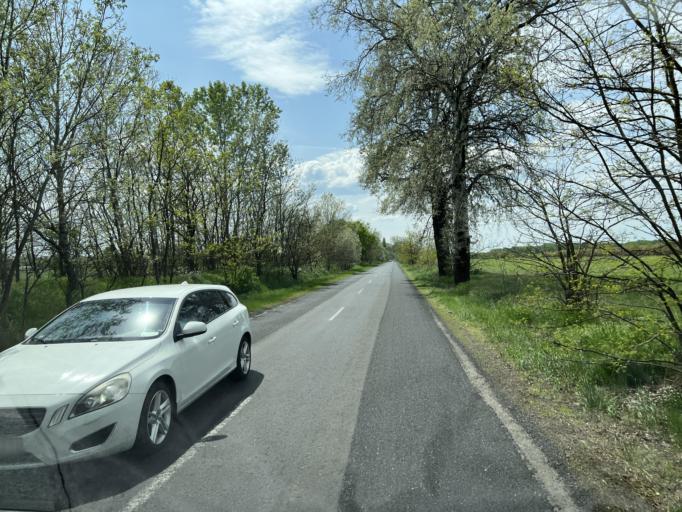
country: HU
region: Pest
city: Cegled
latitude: 47.1473
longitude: 19.7535
